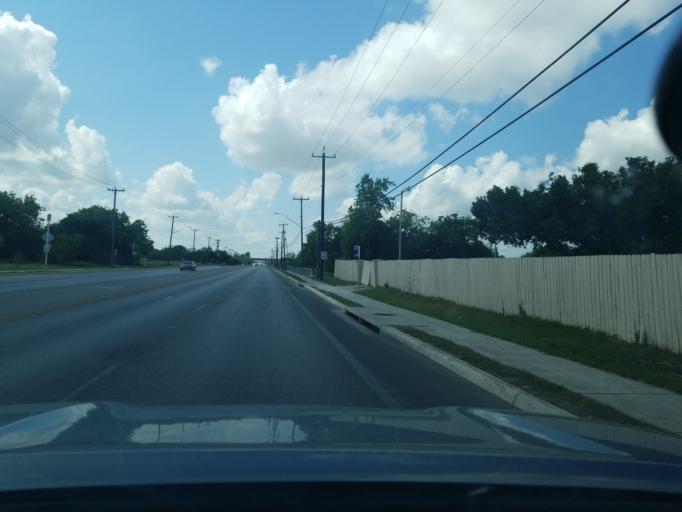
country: US
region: Texas
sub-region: Bexar County
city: Lackland Air Force Base
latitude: 29.3252
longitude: -98.5327
